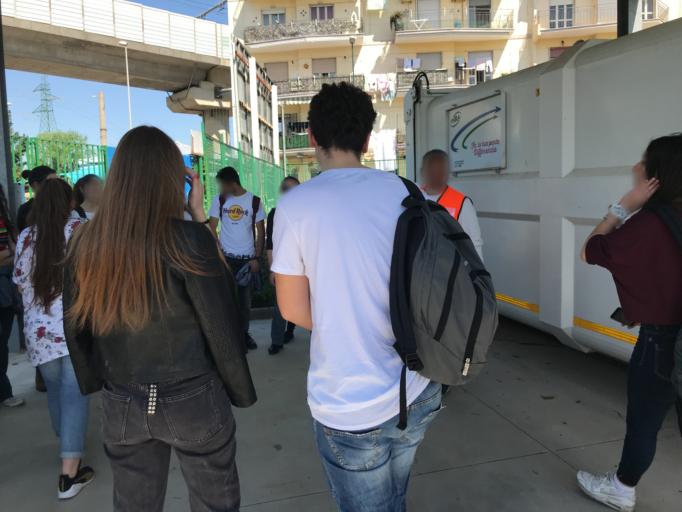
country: IT
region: Campania
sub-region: Provincia di Napoli
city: Mugnano di Napoli
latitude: 40.8938
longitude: 14.2270
